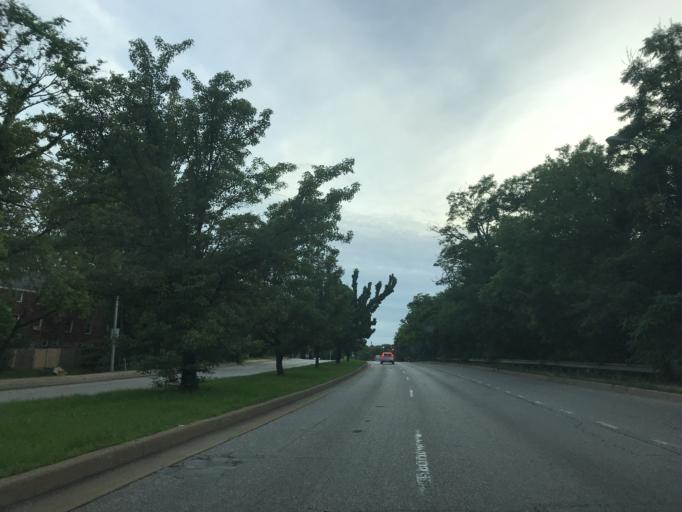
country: US
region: Maryland
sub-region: Baltimore County
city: Towson
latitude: 39.3651
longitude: -76.6136
